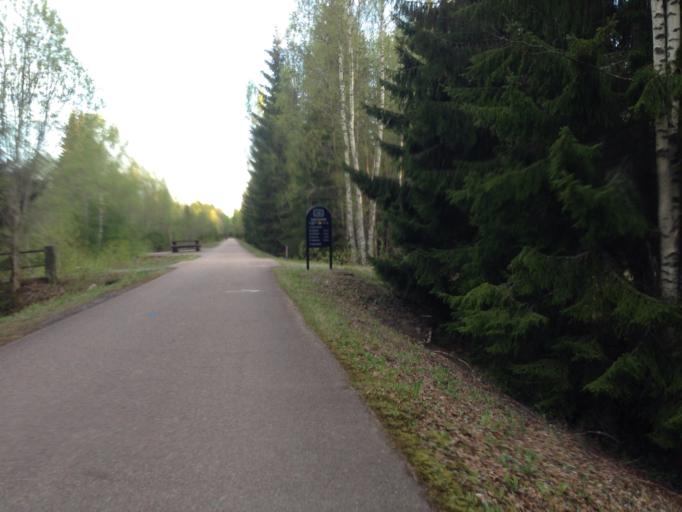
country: SE
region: Dalarna
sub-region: Ludvika Kommun
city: Grangesberg
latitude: 60.1316
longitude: 15.0704
